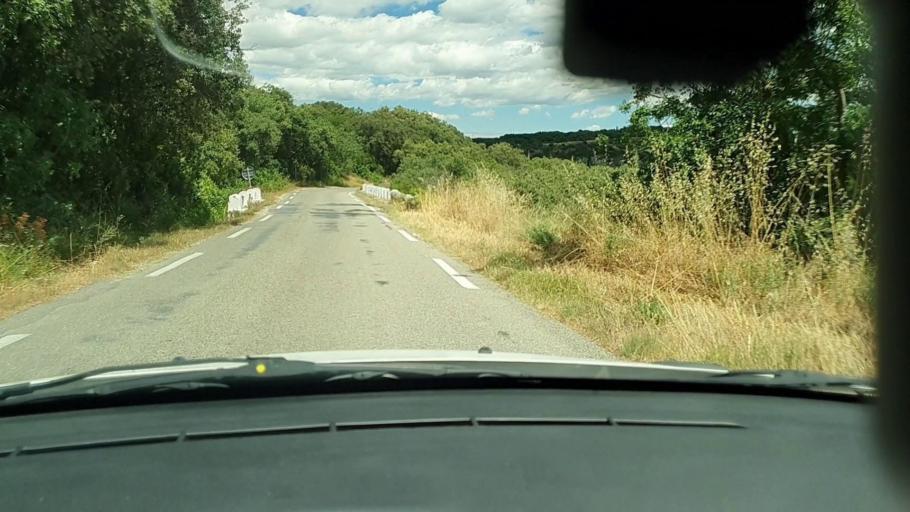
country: FR
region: Languedoc-Roussillon
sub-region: Departement du Gard
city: Ledenon
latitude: 43.9503
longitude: 4.4853
